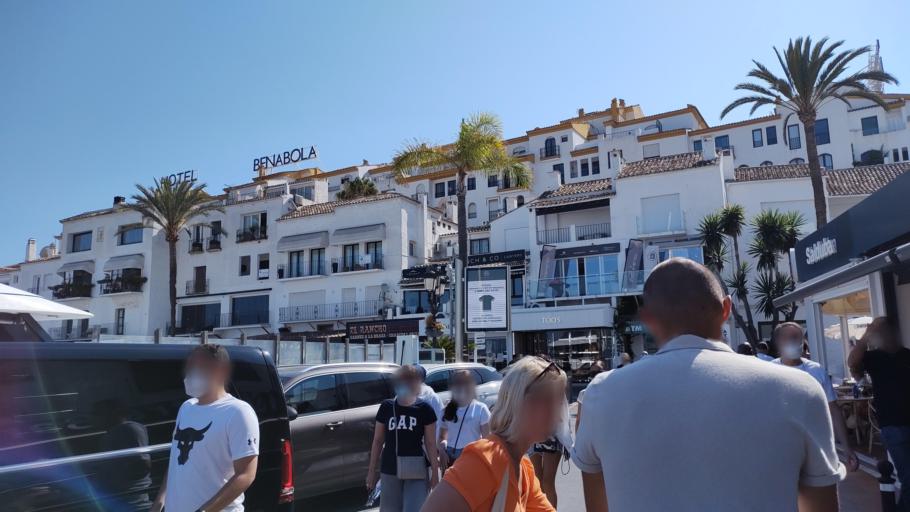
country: ES
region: Andalusia
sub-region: Provincia de Malaga
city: Marbella
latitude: 36.4862
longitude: -4.9542
